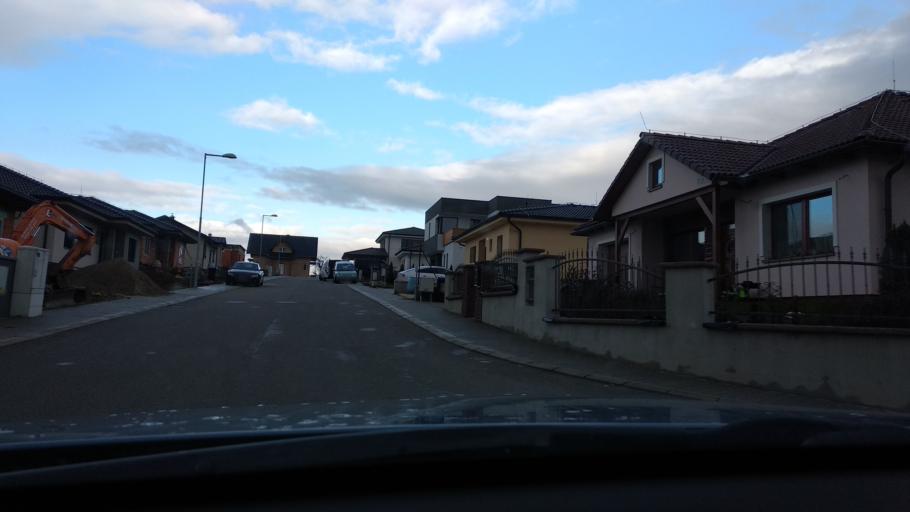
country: SK
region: Trenciansky
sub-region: Okres Trencin
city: Trencin
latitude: 48.8469
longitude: 18.0380
